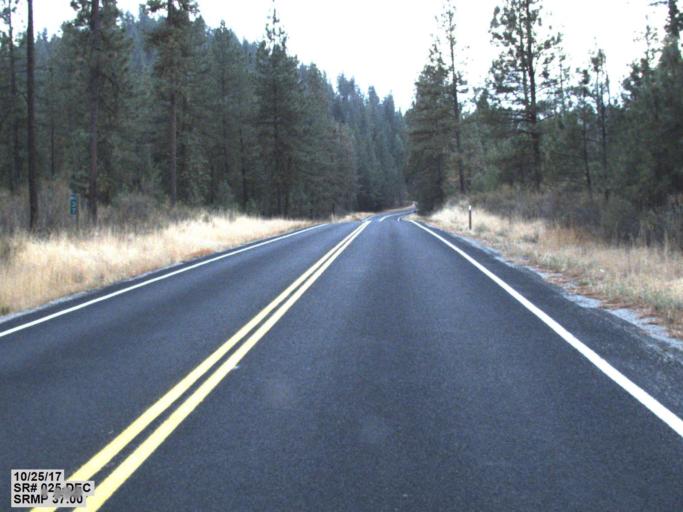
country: US
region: Washington
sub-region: Lincoln County
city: Davenport
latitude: 48.0609
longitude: -118.2158
